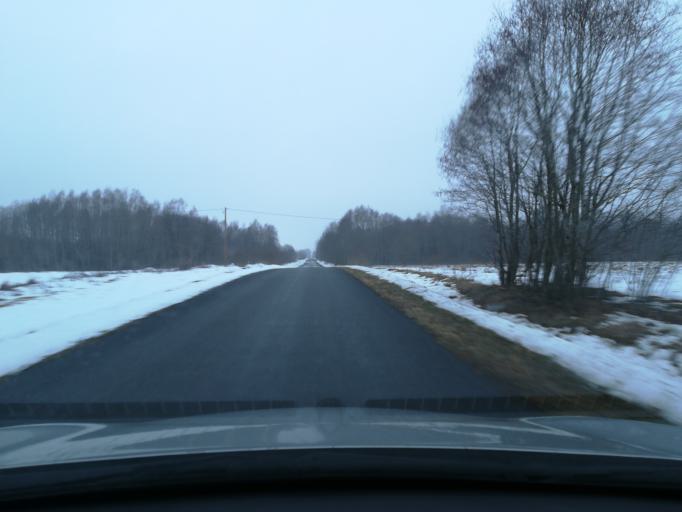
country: EE
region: Harju
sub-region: Raasiku vald
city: Raasiku
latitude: 59.3406
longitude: 25.2292
